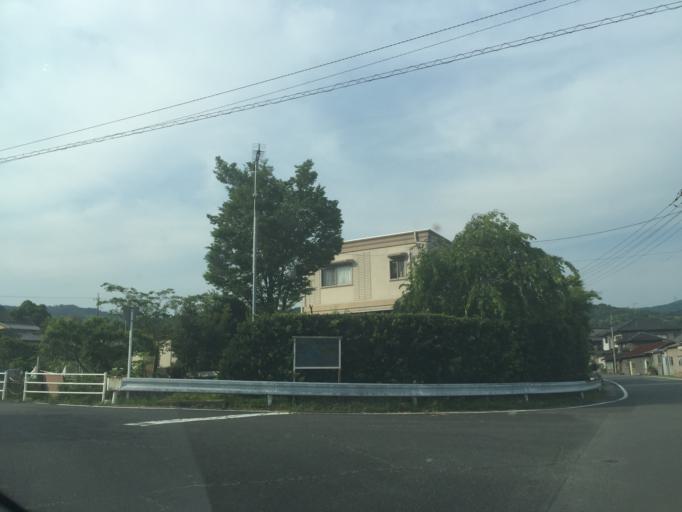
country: JP
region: Shizuoka
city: Mori
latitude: 34.8354
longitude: 137.9653
